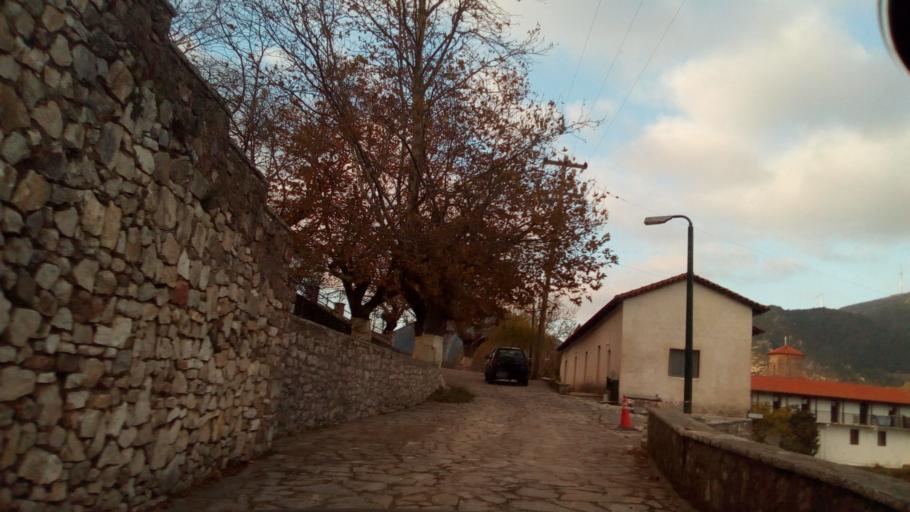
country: GR
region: West Greece
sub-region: Nomos Aitolias kai Akarnanias
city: Nafpaktos
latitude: 38.4336
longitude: 21.8209
